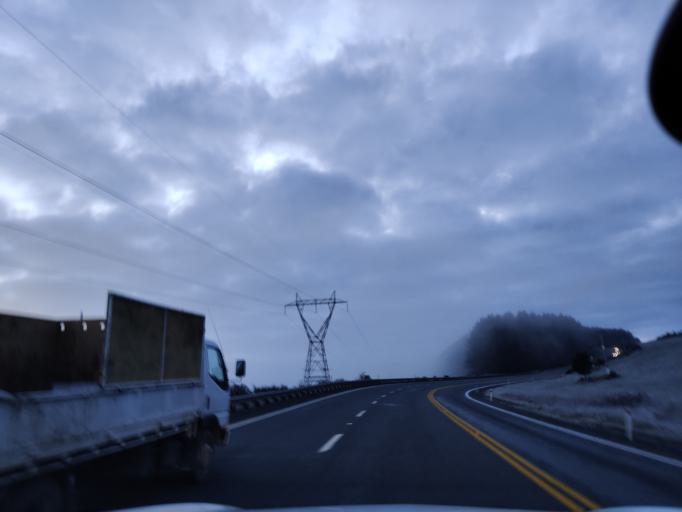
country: NZ
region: Waikato
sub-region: South Waikato District
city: Tokoroa
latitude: -38.3960
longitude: 176.0366
